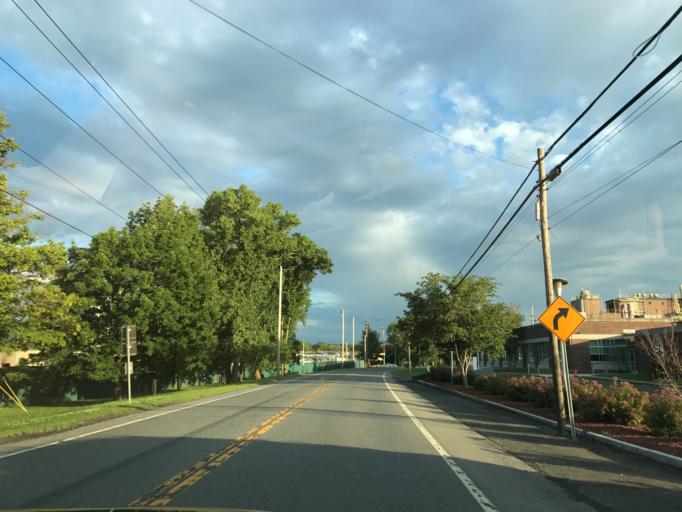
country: US
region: New York
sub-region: Saratoga County
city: Waterford
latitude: 42.8170
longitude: -73.6653
